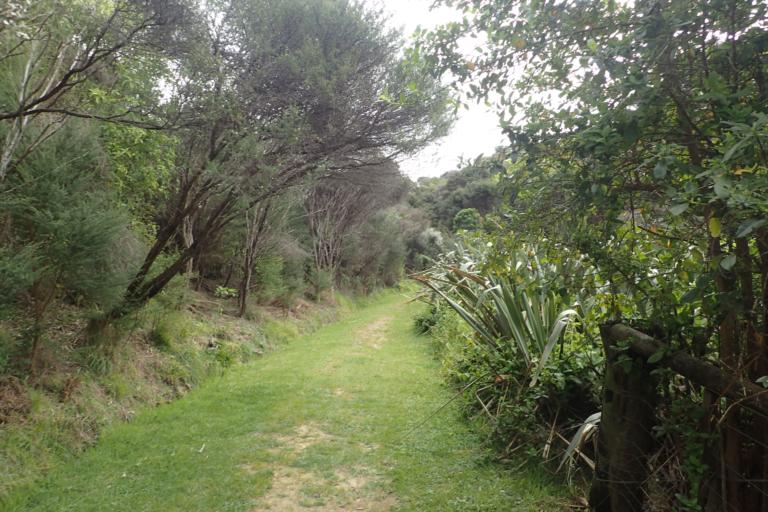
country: NZ
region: Auckland
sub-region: Auckland
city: Pakuranga
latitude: -36.7850
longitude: 174.9988
